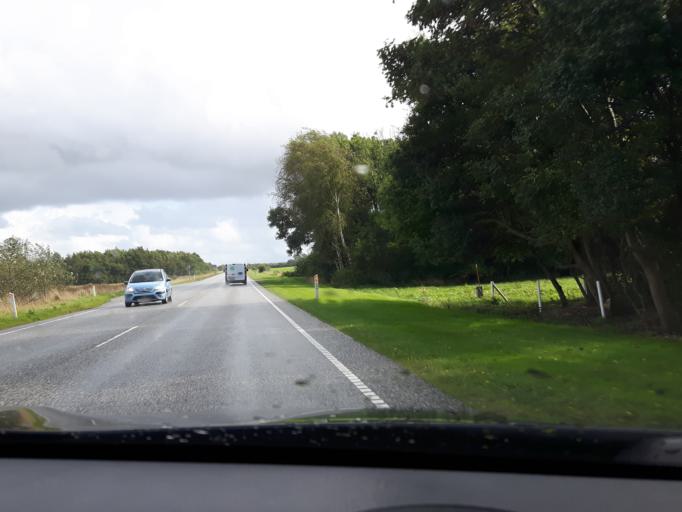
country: DK
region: Central Jutland
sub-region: Holstebro Kommune
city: Holstebro
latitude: 56.3143
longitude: 8.6891
